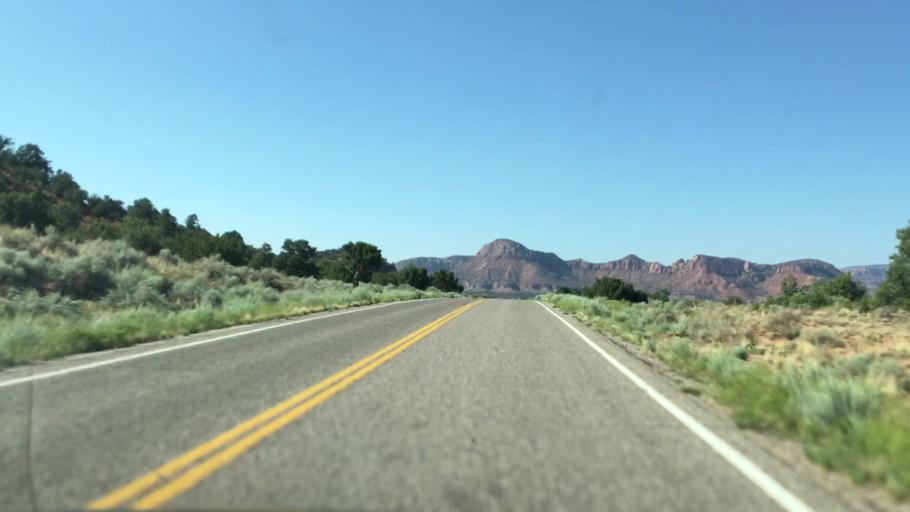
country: US
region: Arizona
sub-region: Coconino County
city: Fredonia
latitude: 36.8729
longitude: -112.7382
